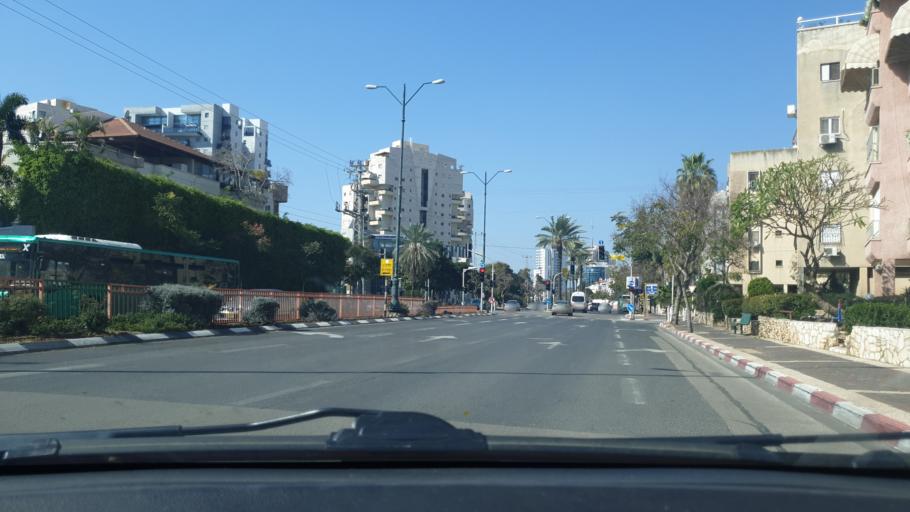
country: IL
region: Central District
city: Rishon LeZiyyon
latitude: 31.9705
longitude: 34.7987
